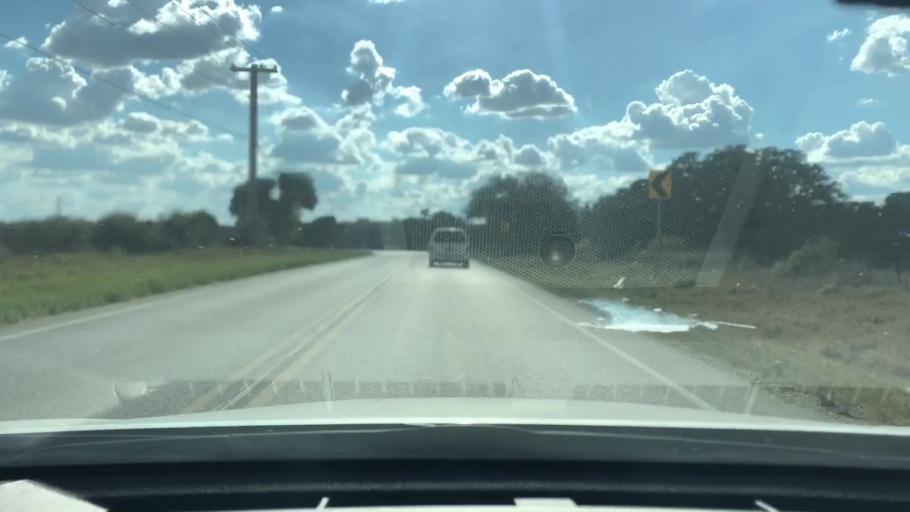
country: US
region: Texas
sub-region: Guadalupe County
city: Northcliff
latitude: 29.6559
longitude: -98.2084
